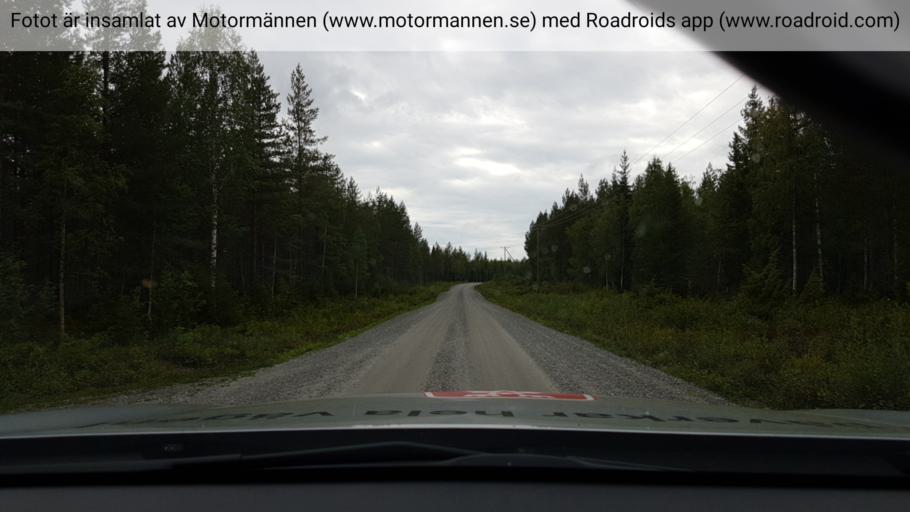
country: SE
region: Vaesterbotten
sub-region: Skelleftea Kommun
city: Langsele
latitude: 64.7287
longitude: 20.2561
